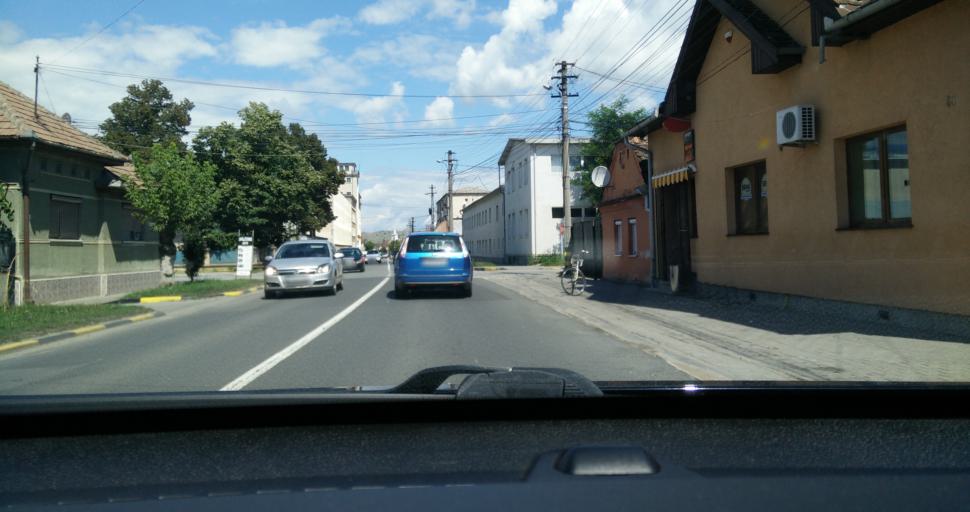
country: RO
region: Alba
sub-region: Municipiul Sebes
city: Sebes
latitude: 45.9490
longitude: 23.5654
